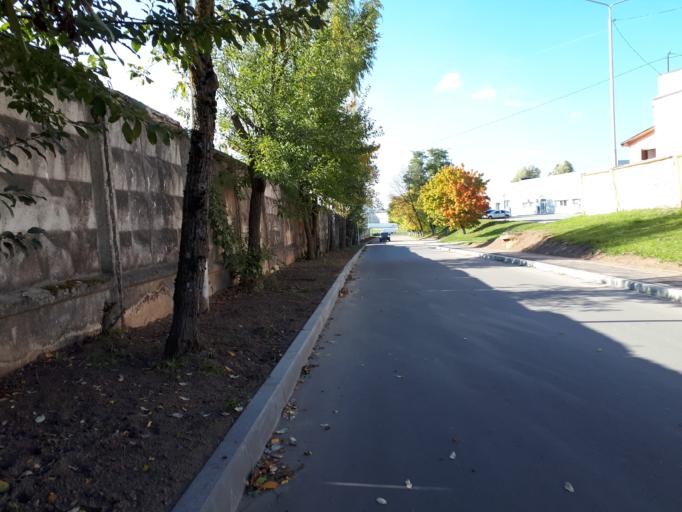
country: BY
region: Vitebsk
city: Vitebsk
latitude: 55.1641
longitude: 30.2428
